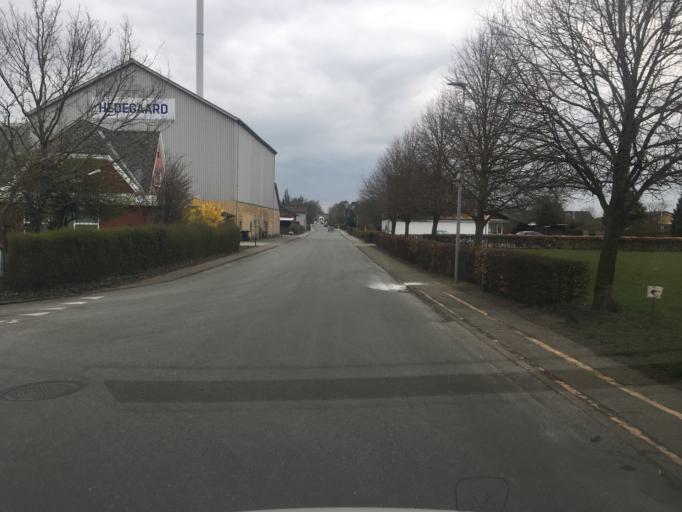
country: DK
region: South Denmark
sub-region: Tonder Kommune
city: Toftlund
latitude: 55.0591
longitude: 9.1060
